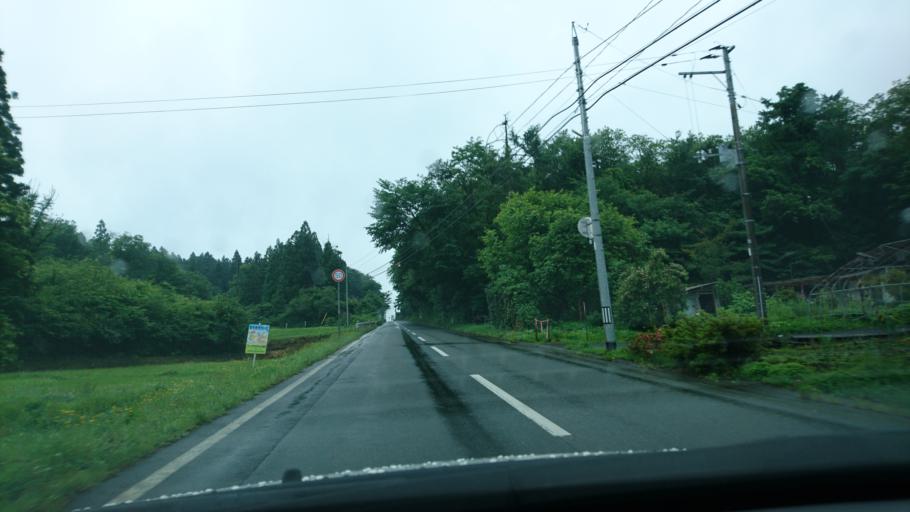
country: JP
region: Iwate
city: Ichinoseki
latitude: 38.9336
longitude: 141.0319
